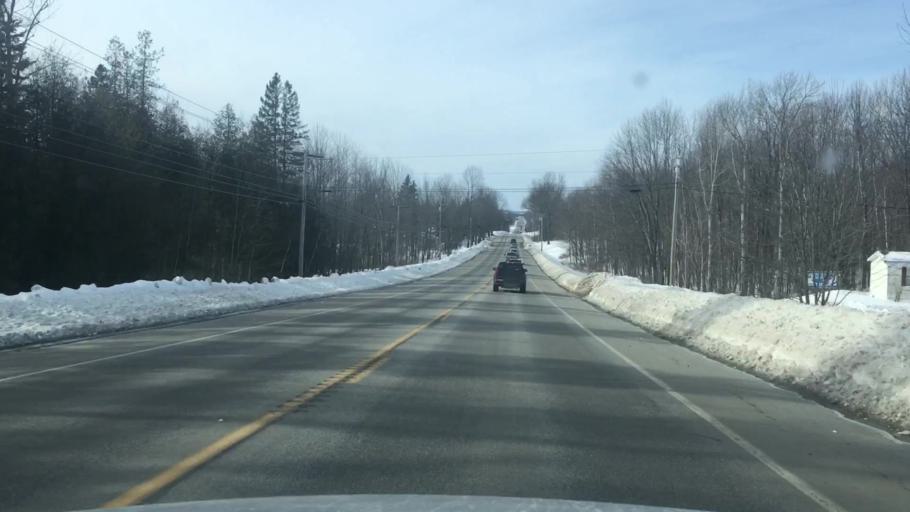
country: US
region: Maine
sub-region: Penobscot County
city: Kenduskeag
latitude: 44.9722
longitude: -68.9793
